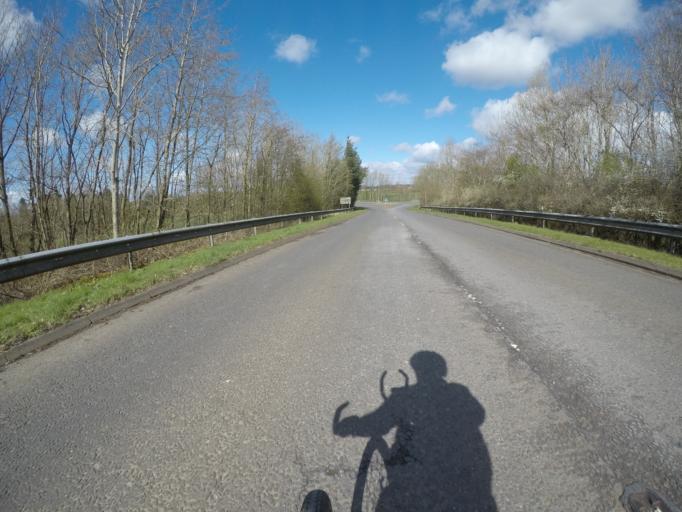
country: GB
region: Scotland
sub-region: North Ayrshire
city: Springside
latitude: 55.6141
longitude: -4.6045
